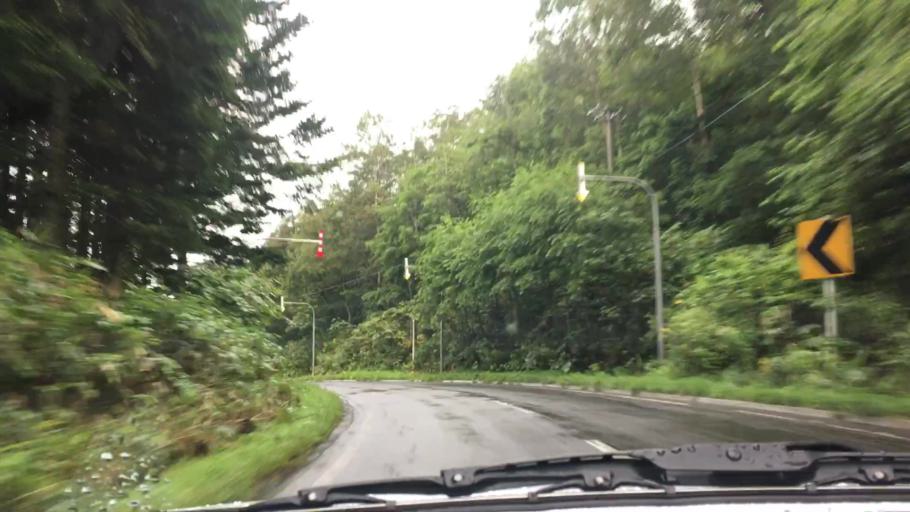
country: JP
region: Hokkaido
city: Niseko Town
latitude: 42.6554
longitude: 140.7407
